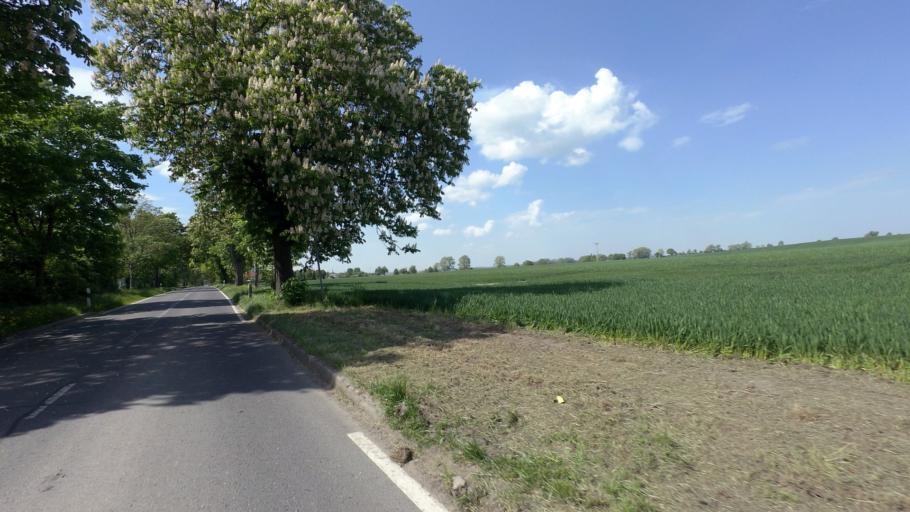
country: DE
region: Mecklenburg-Vorpommern
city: Mollenhagen
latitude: 53.5810
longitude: 12.8736
